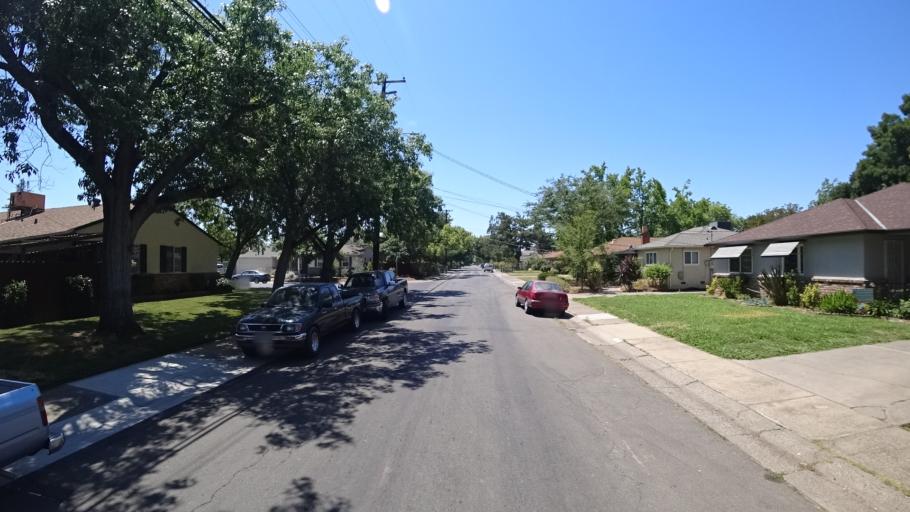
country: US
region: California
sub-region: Sacramento County
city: Parkway
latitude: 38.5369
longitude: -121.4386
